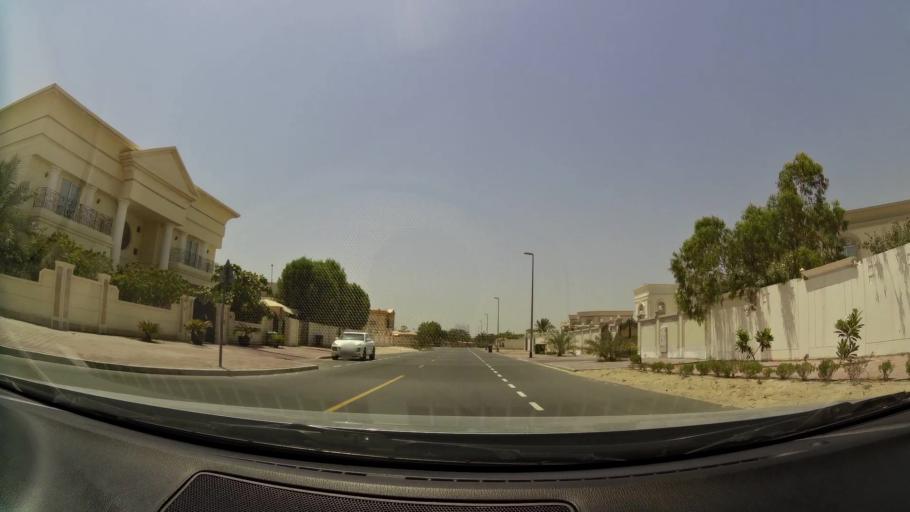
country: AE
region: Dubai
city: Dubai
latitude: 25.0925
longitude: 55.2160
